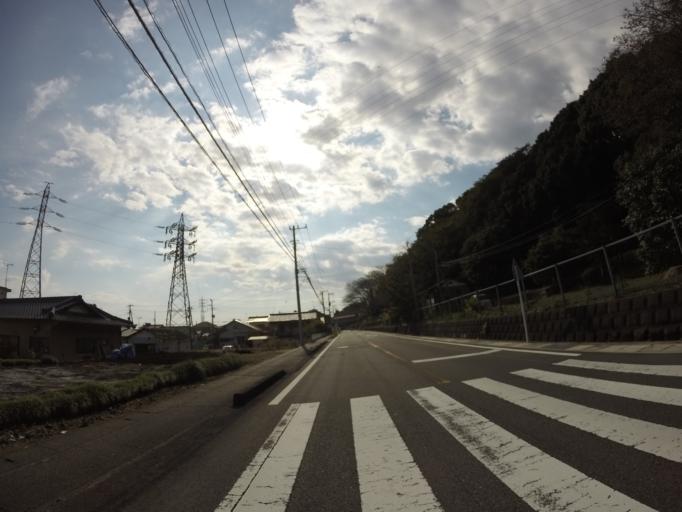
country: JP
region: Shizuoka
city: Fujinomiya
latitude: 35.1793
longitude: 138.6386
